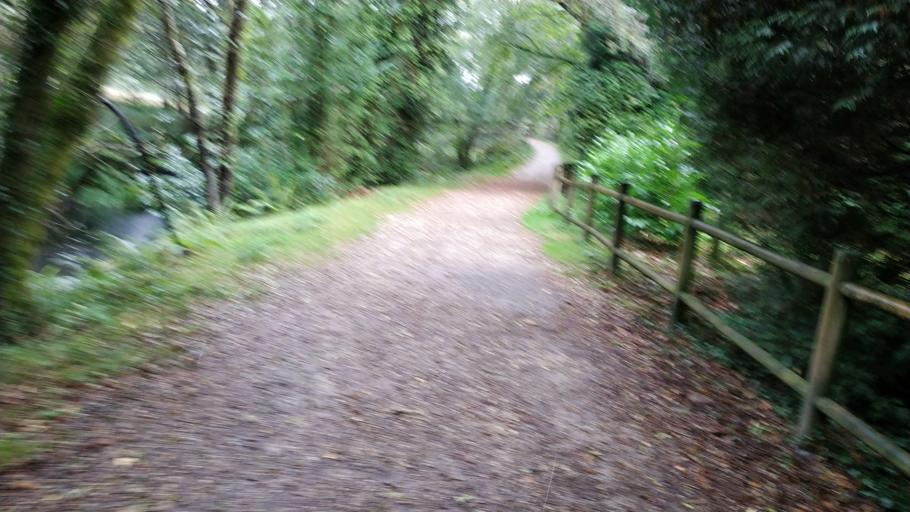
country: ES
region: Galicia
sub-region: Provincia da Coruna
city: Negreira
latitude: 42.9098
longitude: -8.7479
